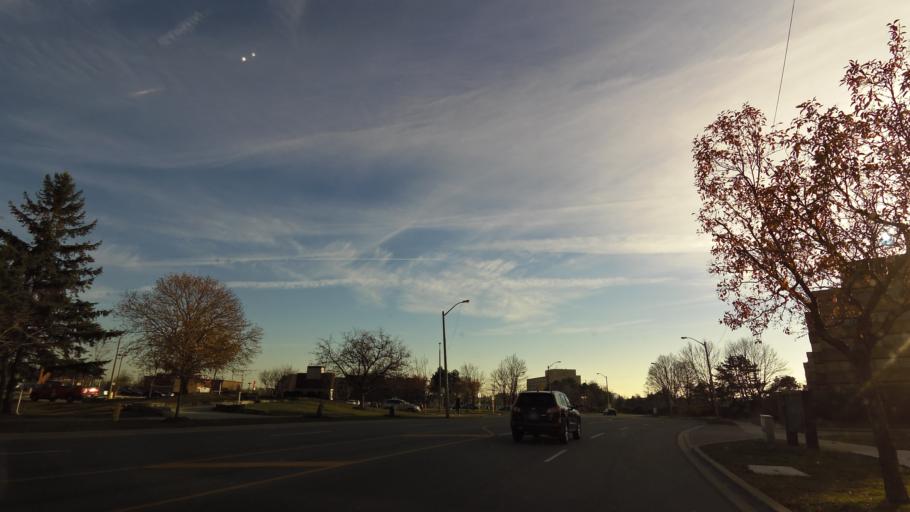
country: CA
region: Ontario
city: Etobicoke
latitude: 43.6900
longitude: -79.5872
